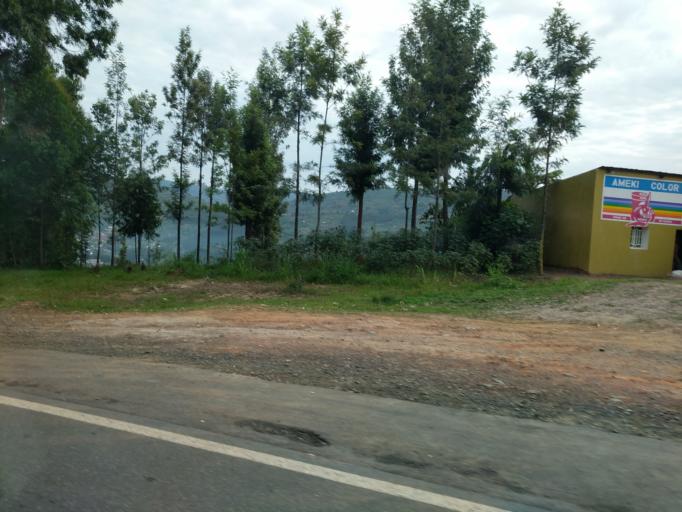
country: RW
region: Kigali
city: Kigali
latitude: -1.7882
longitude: 29.9303
